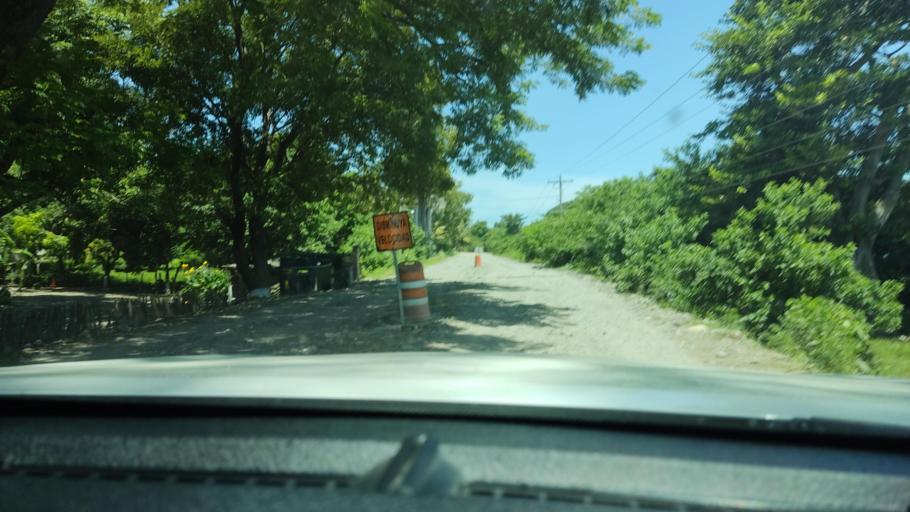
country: SV
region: Ahuachapan
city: San Francisco Menendez
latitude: 13.7842
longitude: -90.1183
